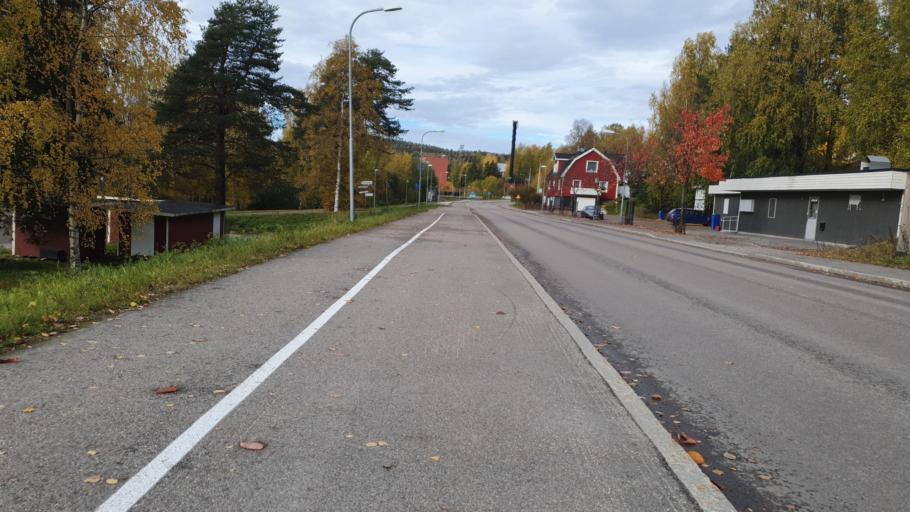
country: SE
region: Vaesternorrland
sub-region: Sundsvalls Kommun
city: Sundsvall
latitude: 62.4101
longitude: 17.2294
